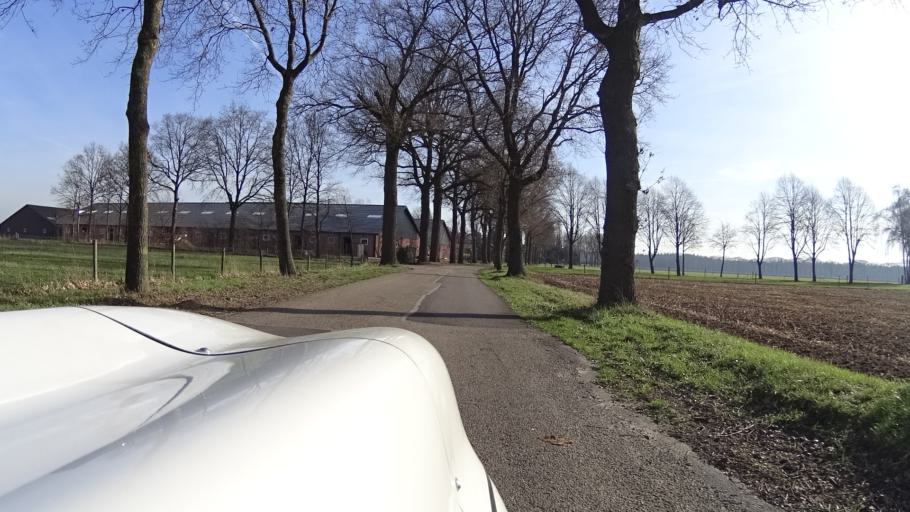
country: NL
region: North Brabant
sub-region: Gemeente Veghel
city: Erp
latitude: 51.5913
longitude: 5.6340
